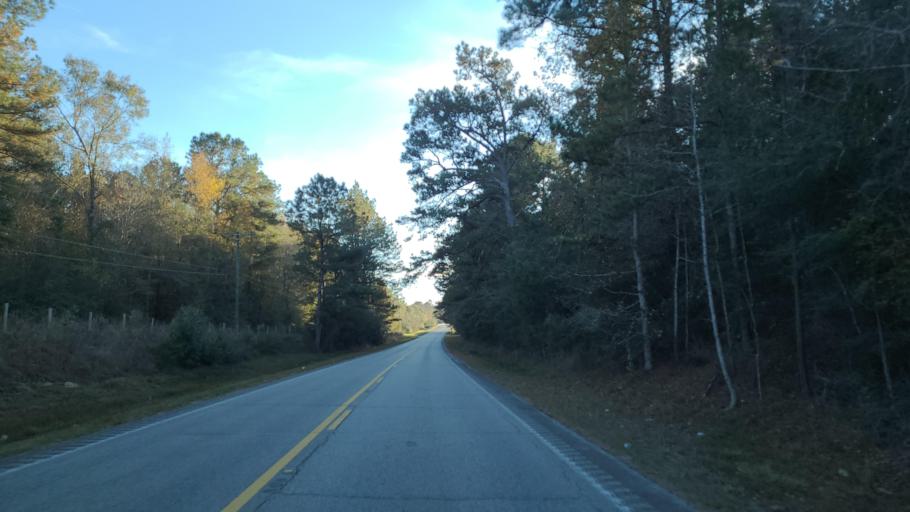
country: US
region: Mississippi
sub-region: Lamar County
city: Purvis
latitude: 31.0775
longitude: -89.4188
